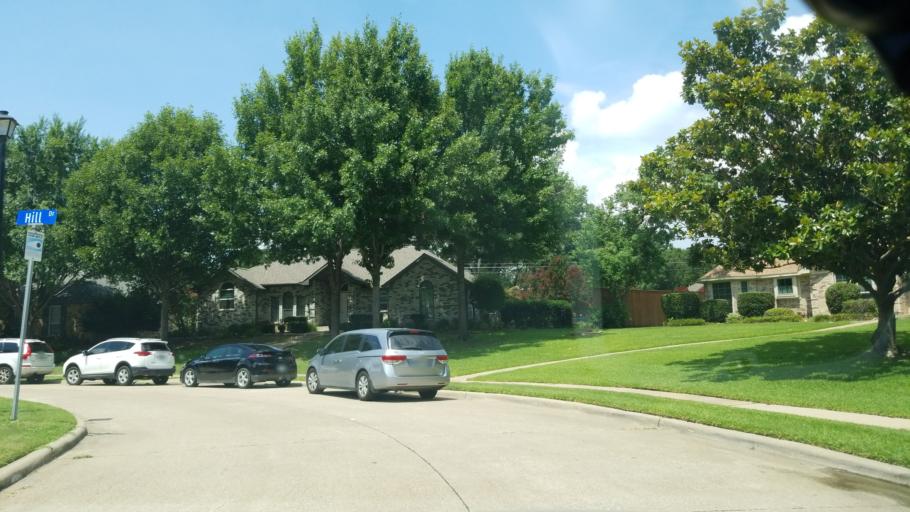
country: US
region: Texas
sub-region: Dallas County
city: Coppell
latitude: 32.9689
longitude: -96.9690
